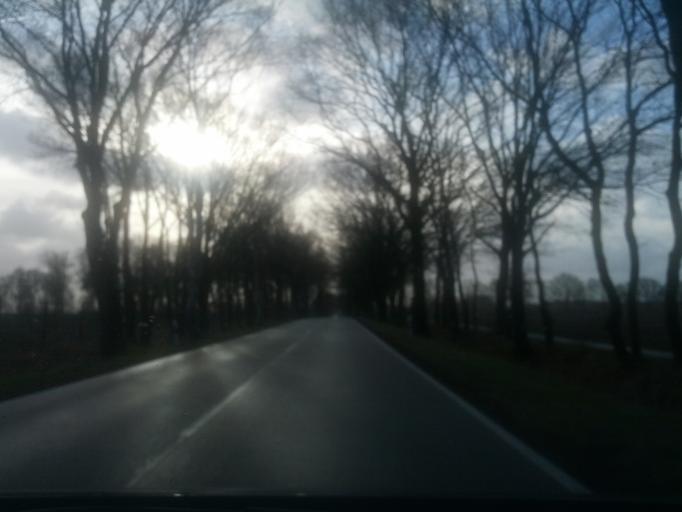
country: DE
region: Lower Saxony
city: Hamersen
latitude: 53.2387
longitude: 9.4849
